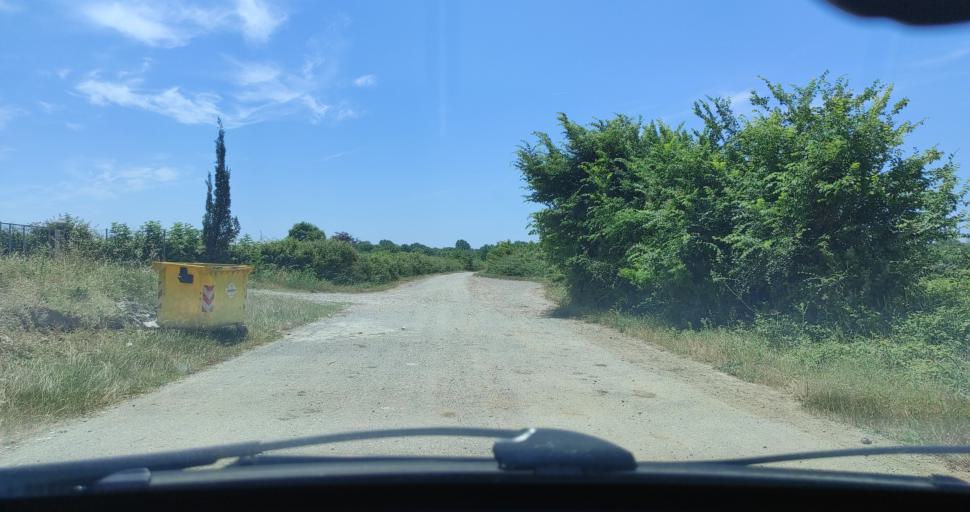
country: AL
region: Shkoder
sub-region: Rrethi i Shkodres
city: Velipoje
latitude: 41.8831
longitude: 19.3846
